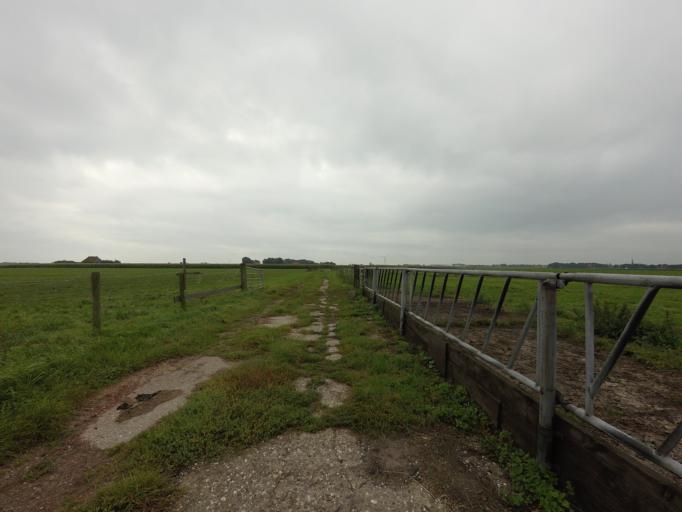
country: NL
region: Friesland
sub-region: Sudwest Fryslan
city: Workum
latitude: 52.9971
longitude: 5.4719
